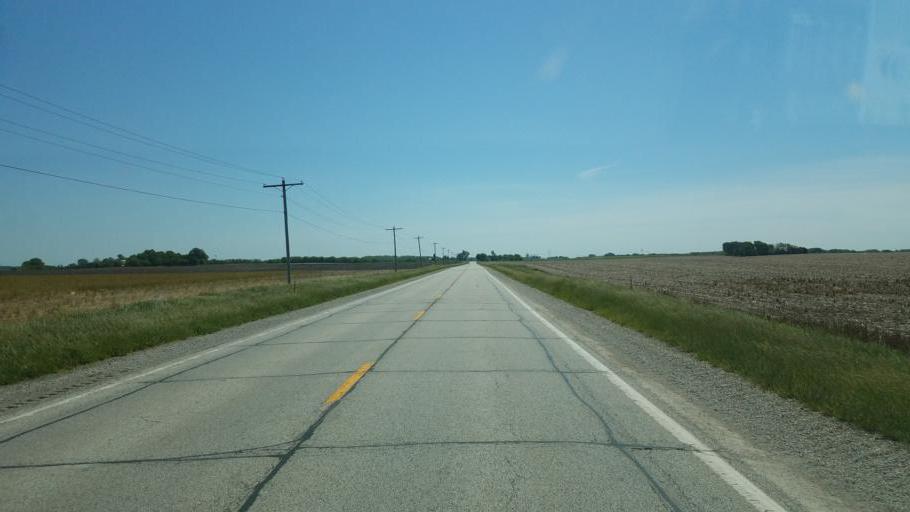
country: US
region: Illinois
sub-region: McLean County
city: Heyworth
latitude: 40.3121
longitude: -89.0482
